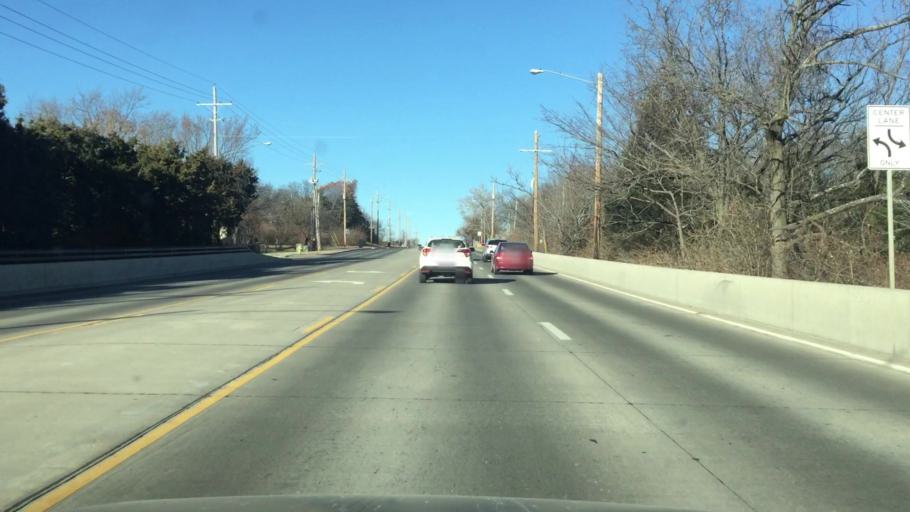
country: US
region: Kansas
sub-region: Douglas County
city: Lawrence
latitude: 38.9587
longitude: -95.2604
